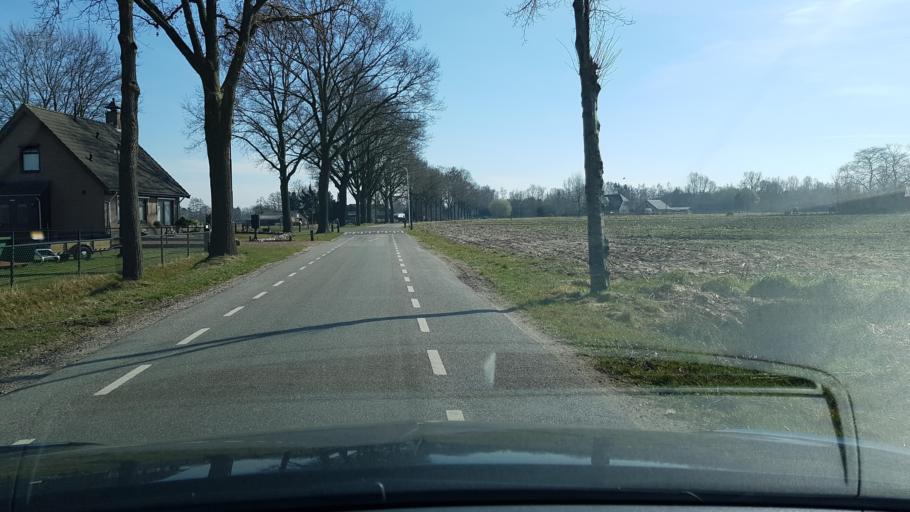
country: NL
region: Gelderland
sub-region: Gemeente Epe
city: Emst
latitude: 52.3051
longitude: 5.9593
